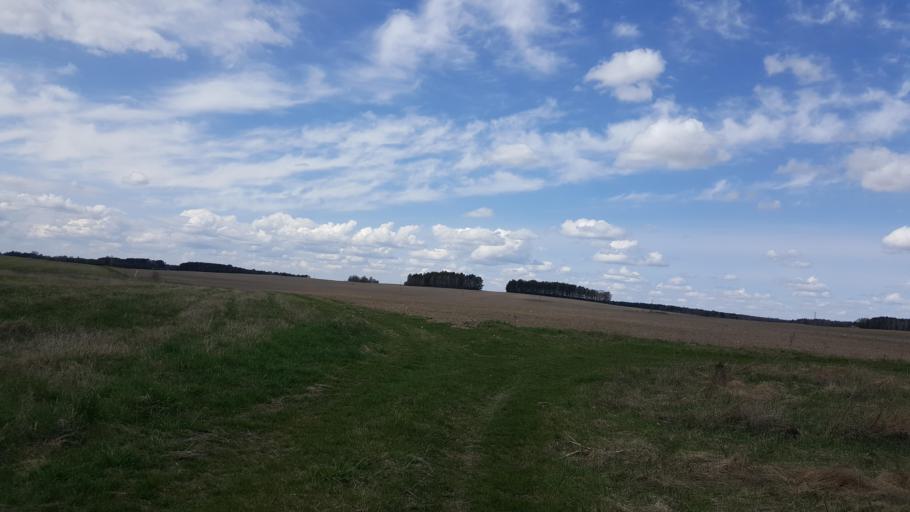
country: BY
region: Brest
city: Kamyanyets
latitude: 52.3509
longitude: 23.7301
